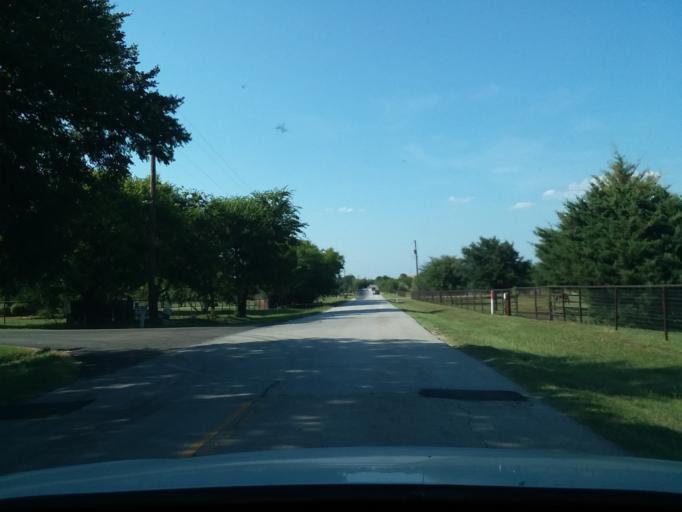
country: US
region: Texas
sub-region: Denton County
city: Bartonville
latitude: 33.0666
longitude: -97.1315
